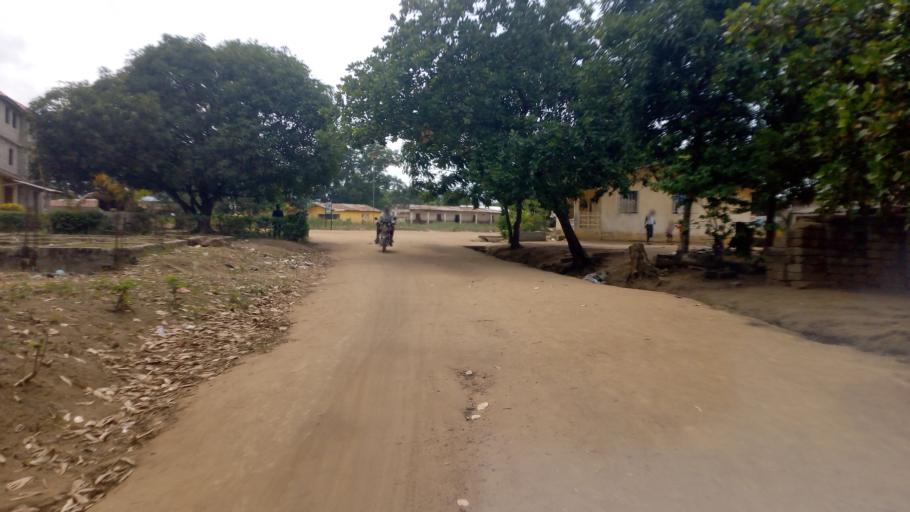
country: SL
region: Western Area
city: Waterloo
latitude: 8.3132
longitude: -13.0648
